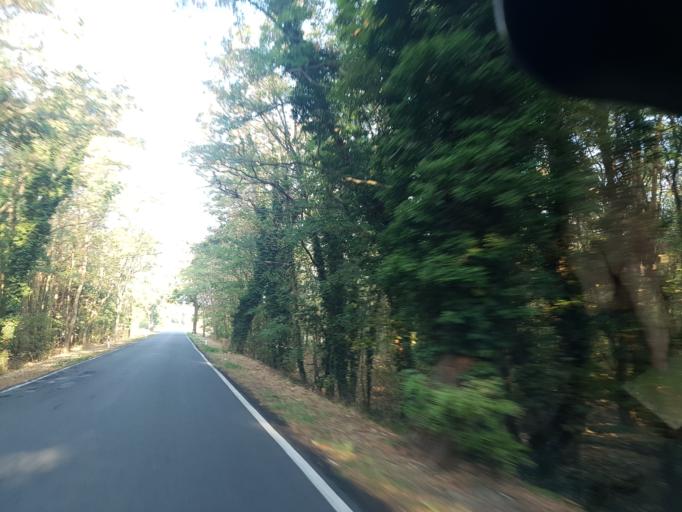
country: DE
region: Saxony-Anhalt
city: Kropstadt
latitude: 51.9858
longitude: 12.6959
